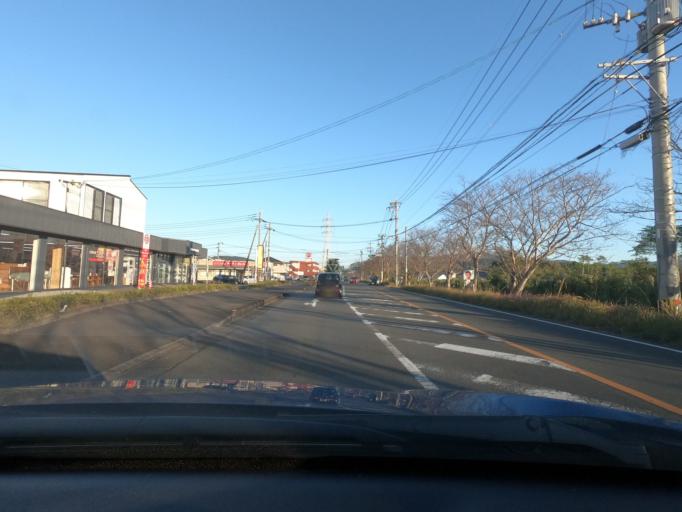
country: JP
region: Kagoshima
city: Satsumasendai
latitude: 31.8095
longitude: 130.3184
